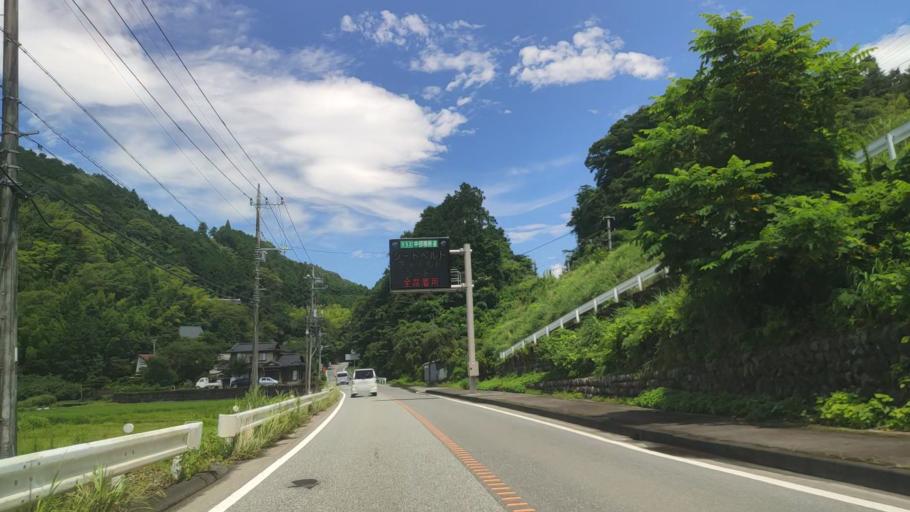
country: JP
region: Shizuoka
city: Fujinomiya
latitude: 35.3439
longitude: 138.4497
